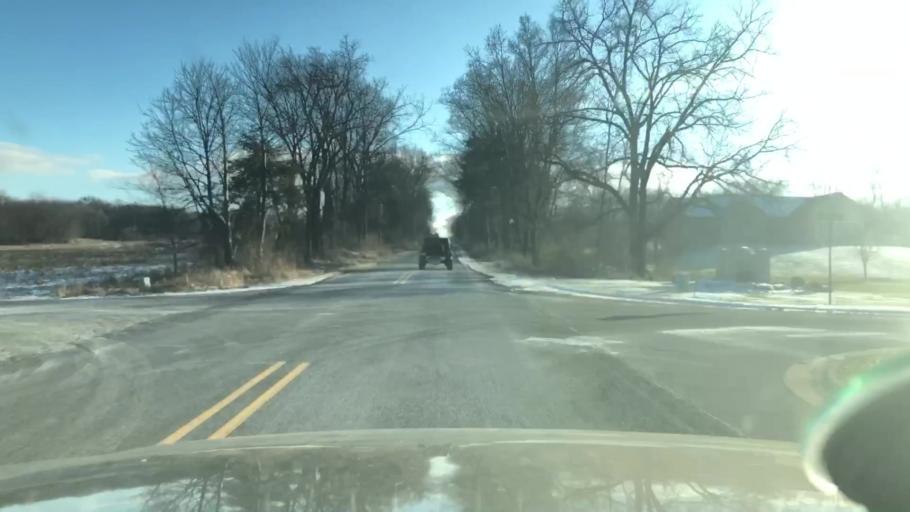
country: US
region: Michigan
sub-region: Jackson County
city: Vandercook Lake
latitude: 42.1303
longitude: -84.4516
